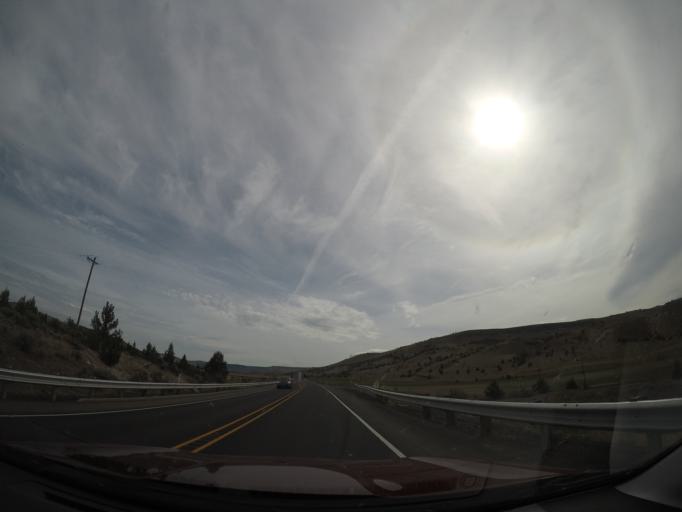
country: US
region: Oregon
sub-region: Jefferson County
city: Madras
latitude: 44.7785
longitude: -120.9669
